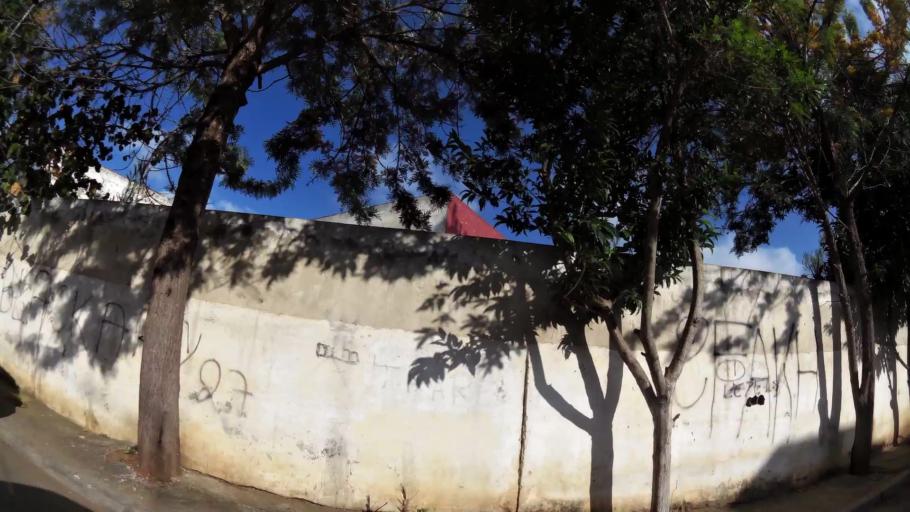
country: MA
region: Rabat-Sale-Zemmour-Zaer
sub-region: Skhirate-Temara
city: Temara
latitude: 33.9548
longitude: -6.8602
